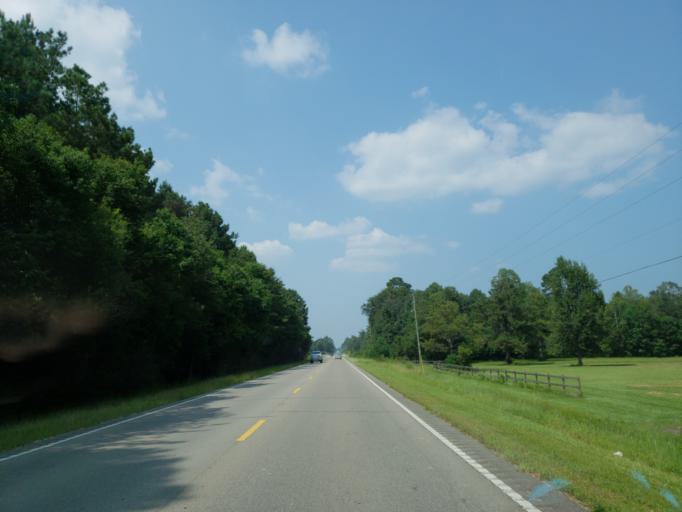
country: US
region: Mississippi
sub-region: Forrest County
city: Glendale
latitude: 31.4617
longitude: -89.2845
